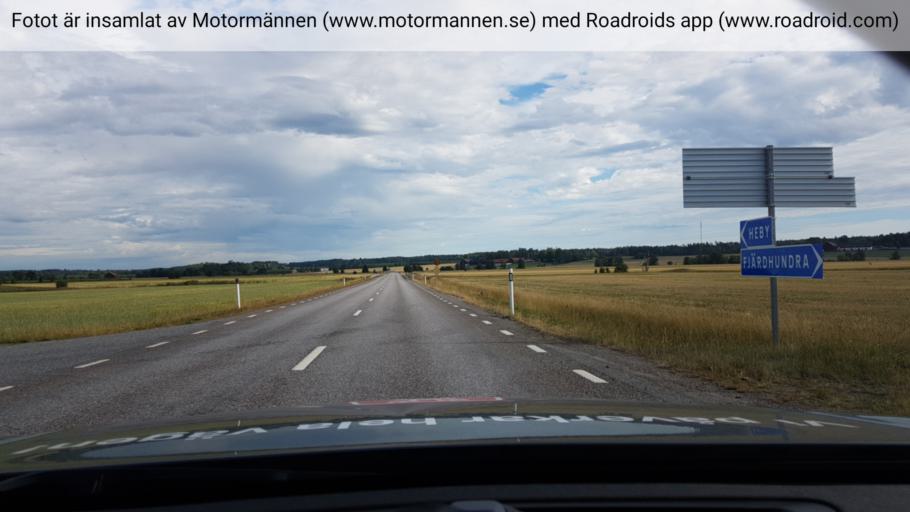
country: SE
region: Uppsala
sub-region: Heby Kommun
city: Morgongava
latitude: 59.8219
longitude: 16.9238
